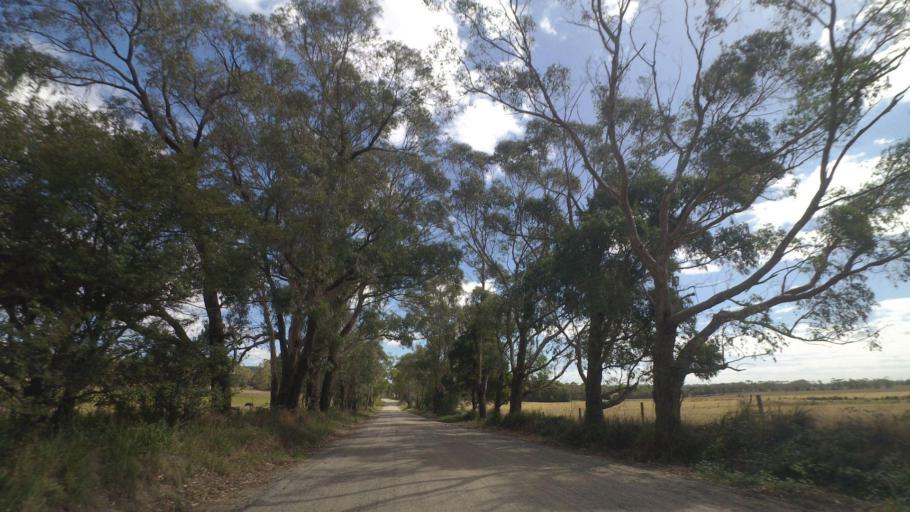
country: AU
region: Victoria
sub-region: Cardinia
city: Bunyip
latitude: -38.3187
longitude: 145.7300
